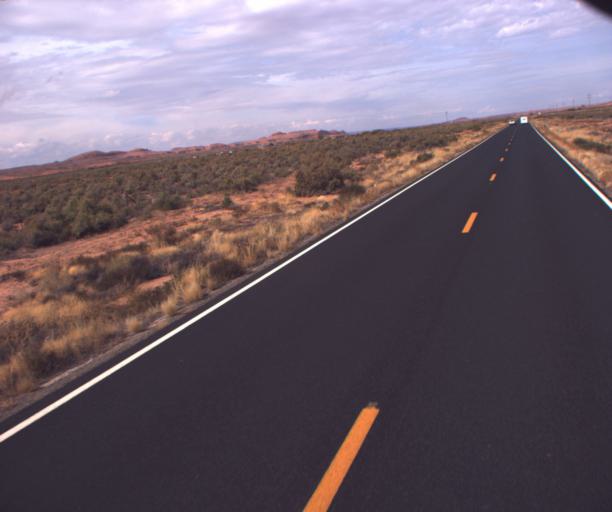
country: US
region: Arizona
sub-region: Apache County
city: Many Farms
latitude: 36.6657
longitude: -109.5974
